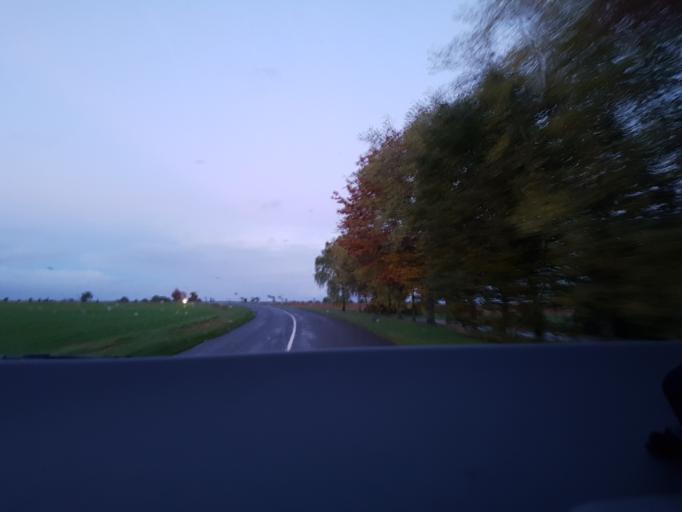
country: FR
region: Poitou-Charentes
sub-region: Departement des Deux-Sevres
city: Lezay
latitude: 46.2491
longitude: -0.0348
